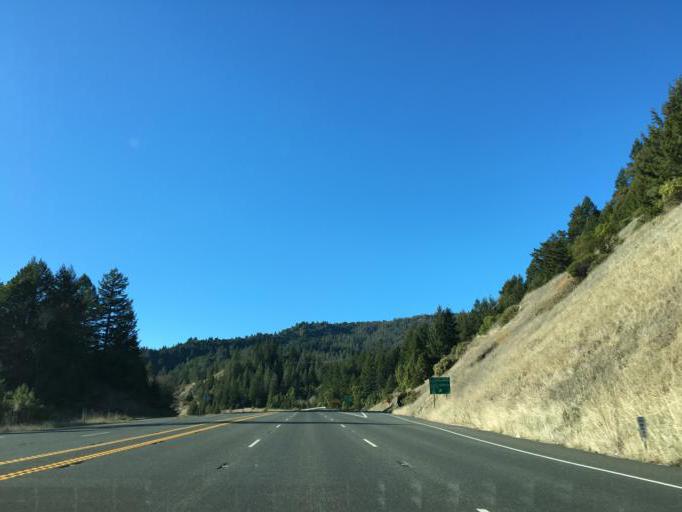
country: US
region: California
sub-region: Mendocino County
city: Laytonville
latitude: 39.8336
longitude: -123.6280
